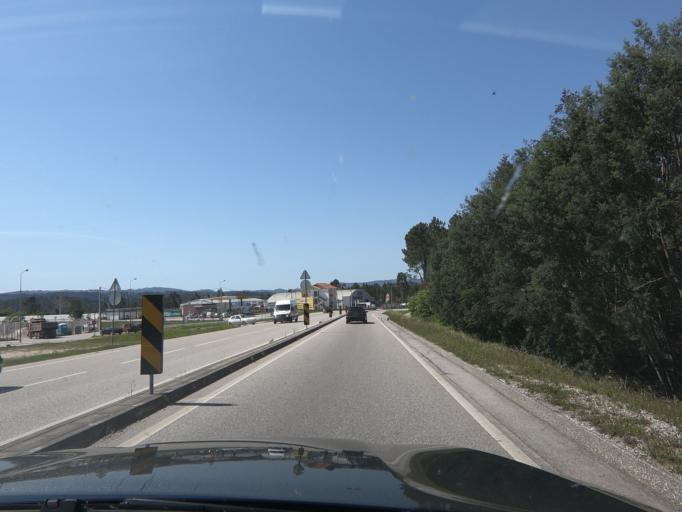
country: PT
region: Coimbra
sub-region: Lousa
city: Lousa
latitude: 40.1294
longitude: -8.2488
